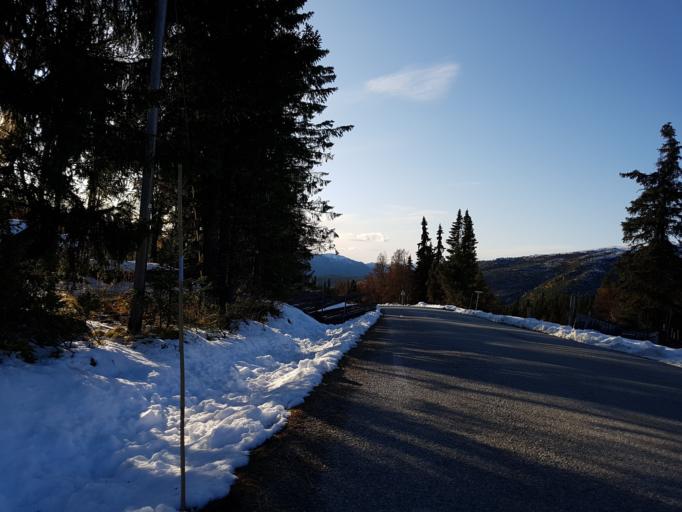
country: NO
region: Oppland
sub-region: Sel
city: Otta
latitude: 61.8093
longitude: 9.6785
